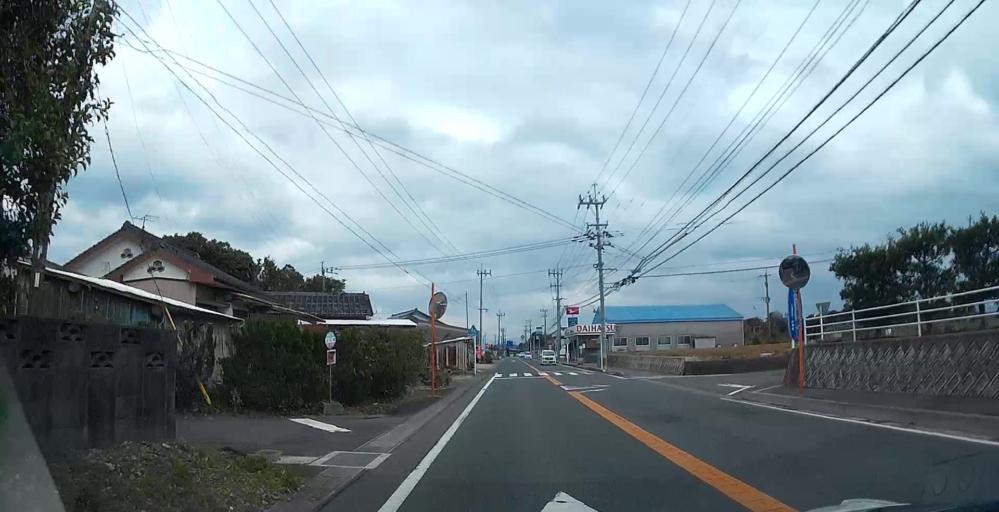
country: JP
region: Kagoshima
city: Akune
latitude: 32.0902
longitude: 130.1829
